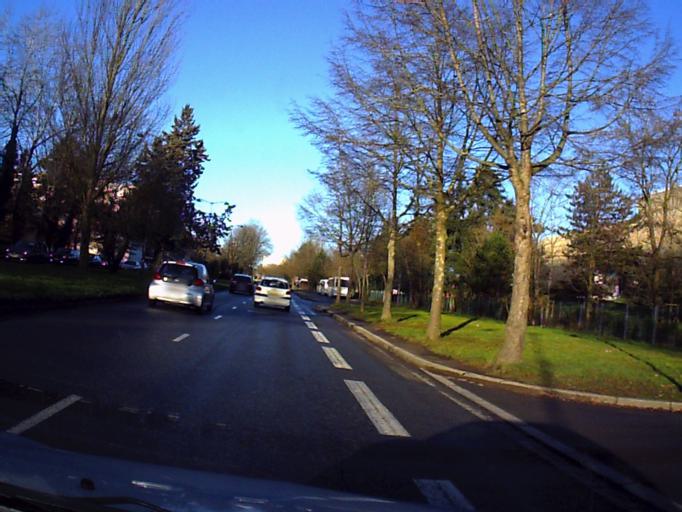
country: FR
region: Brittany
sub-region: Departement d'Ille-et-Vilaine
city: Saint-Gregoire
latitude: 48.1247
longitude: -1.7042
